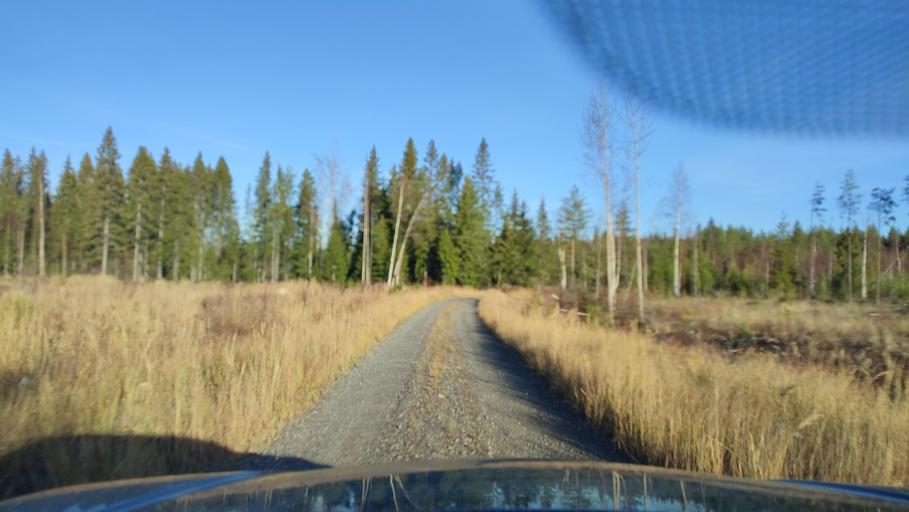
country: FI
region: Southern Ostrobothnia
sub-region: Suupohja
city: Karijoki
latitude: 62.1936
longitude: 21.6064
